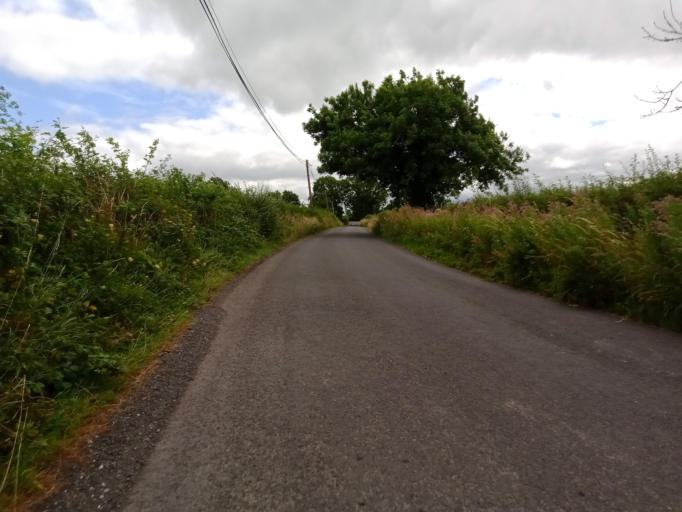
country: IE
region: Leinster
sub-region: Kilkenny
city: Callan
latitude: 52.5642
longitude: -7.3754
